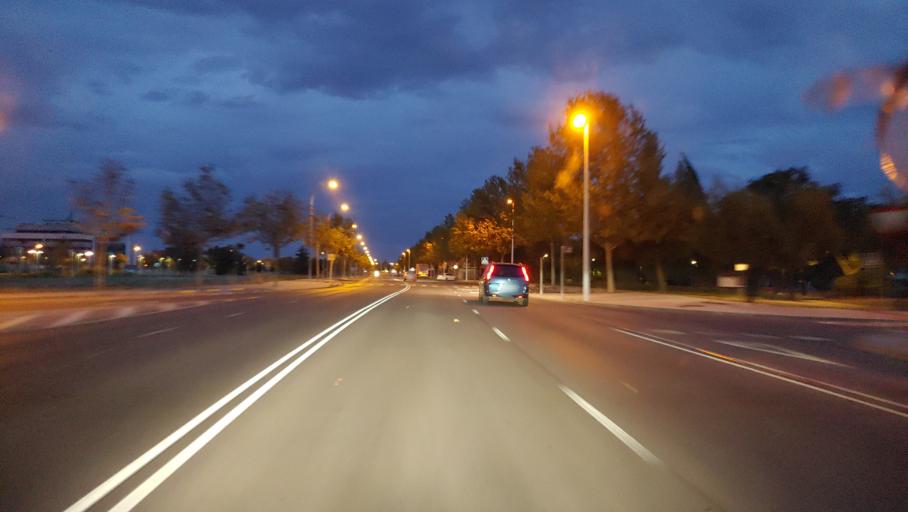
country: ES
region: Castille-La Mancha
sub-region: Provincia de Ciudad Real
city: Ciudad Real
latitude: 38.9704
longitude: -3.9224
